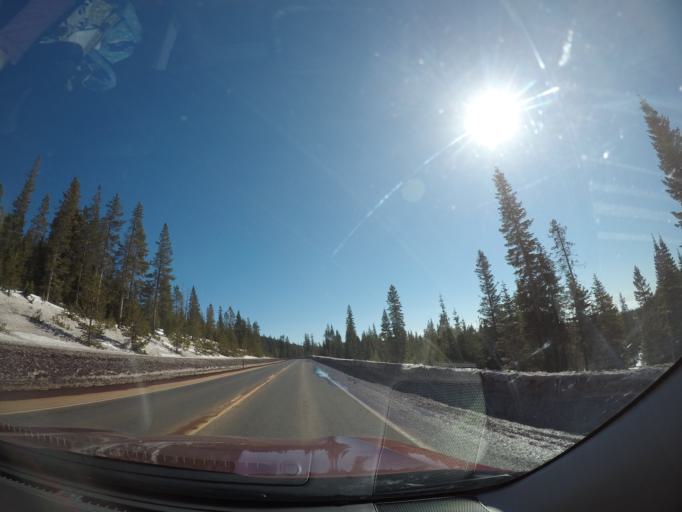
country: US
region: Oregon
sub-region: Deschutes County
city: Sunriver
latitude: 43.9834
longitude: -121.5990
